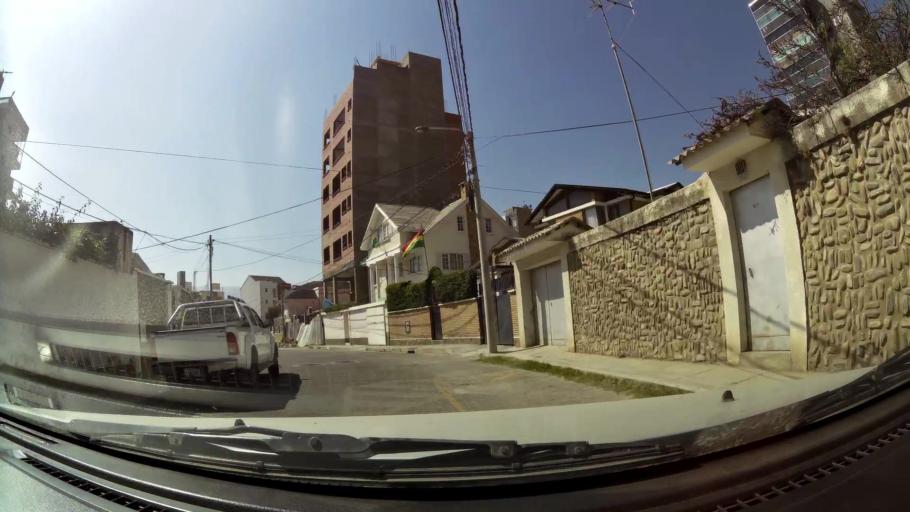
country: BO
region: La Paz
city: La Paz
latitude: -16.5443
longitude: -68.0790
